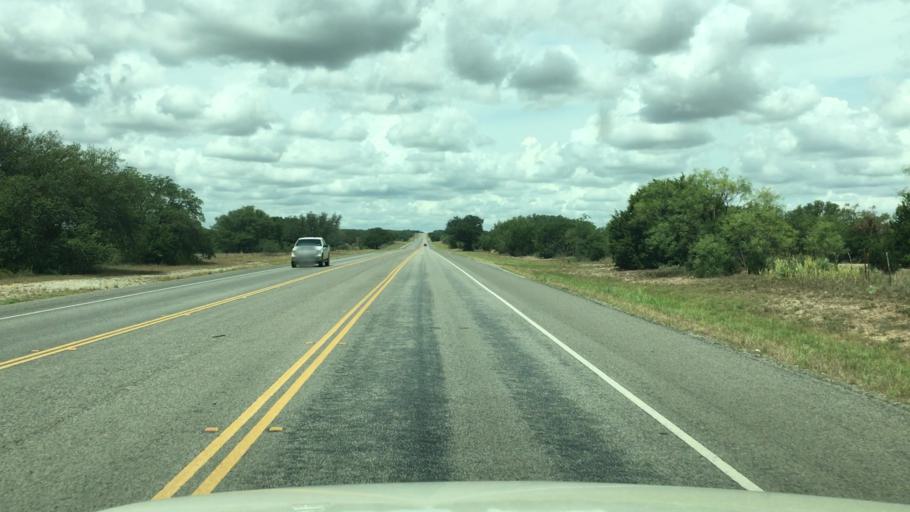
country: US
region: Texas
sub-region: McCulloch County
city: Brady
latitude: 31.0204
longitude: -99.2146
